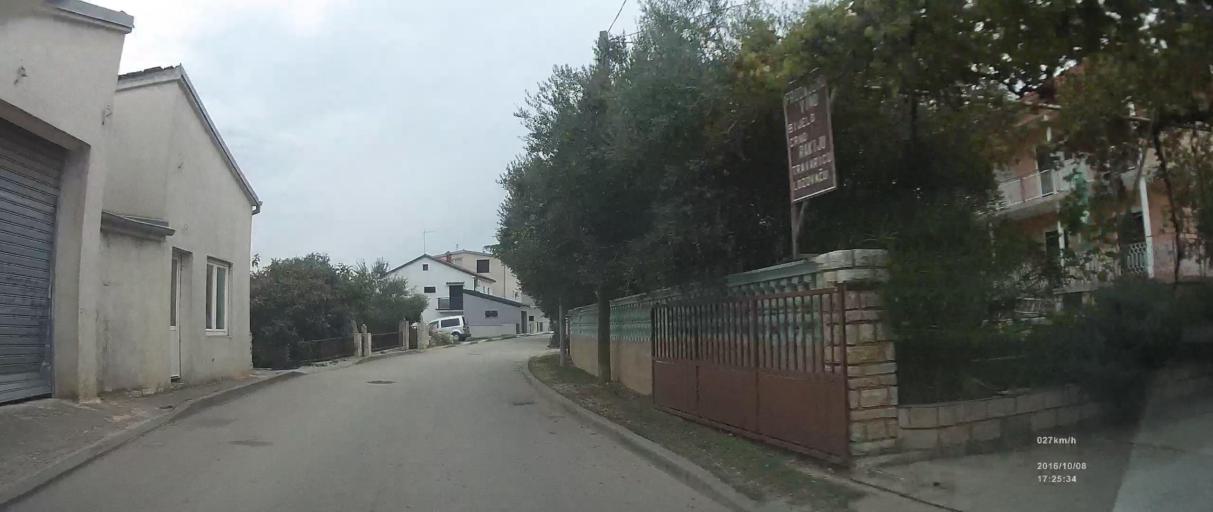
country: HR
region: Zadarska
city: Pakostane
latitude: 43.9108
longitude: 15.5051
